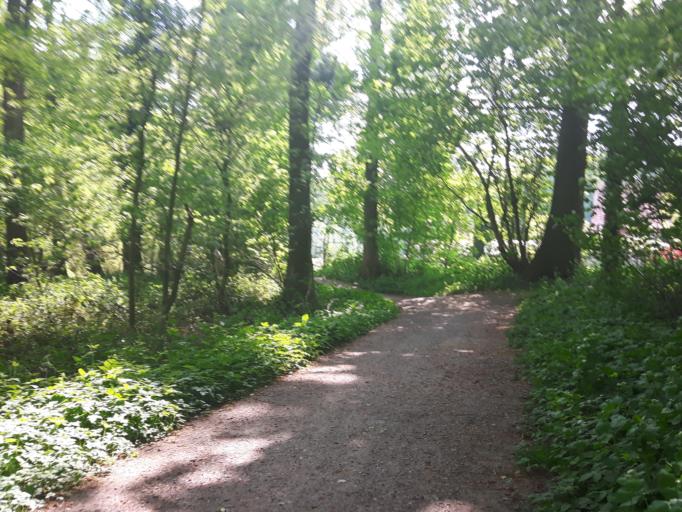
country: NL
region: Overijssel
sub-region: Gemeente Enschede
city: Enschede
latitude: 52.1334
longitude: 6.8754
